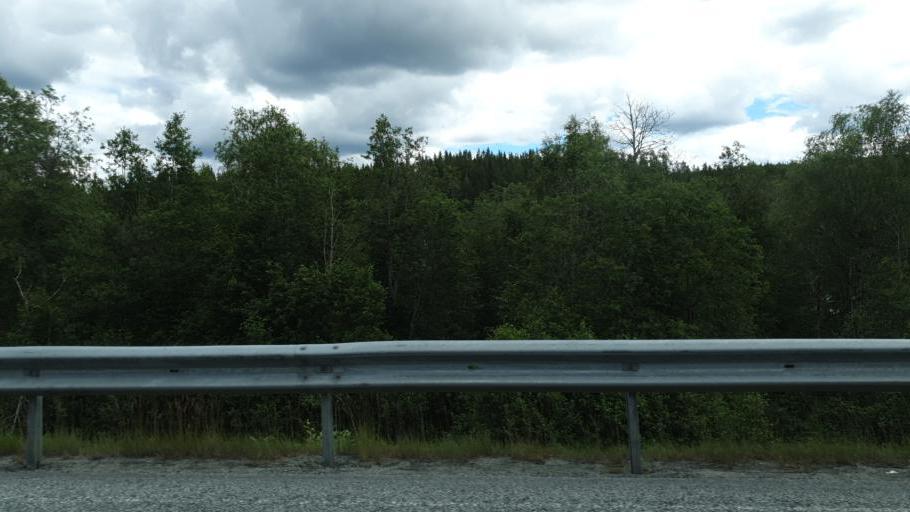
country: NO
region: Sor-Trondelag
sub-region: Rennebu
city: Berkak
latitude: 62.8744
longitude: 10.0855
